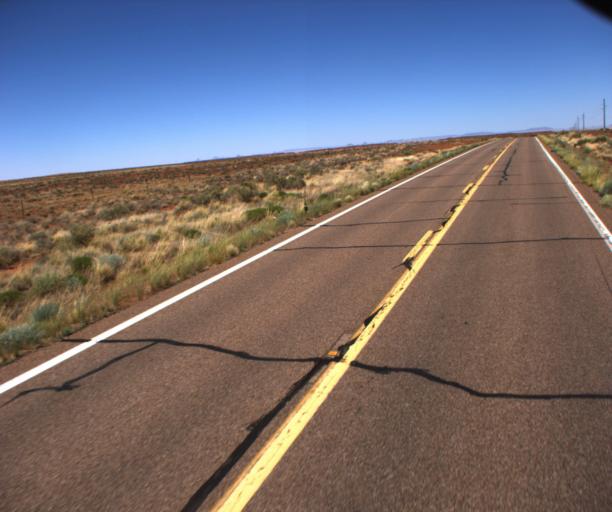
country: US
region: Arizona
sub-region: Coconino County
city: LeChee
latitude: 34.9161
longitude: -110.8276
